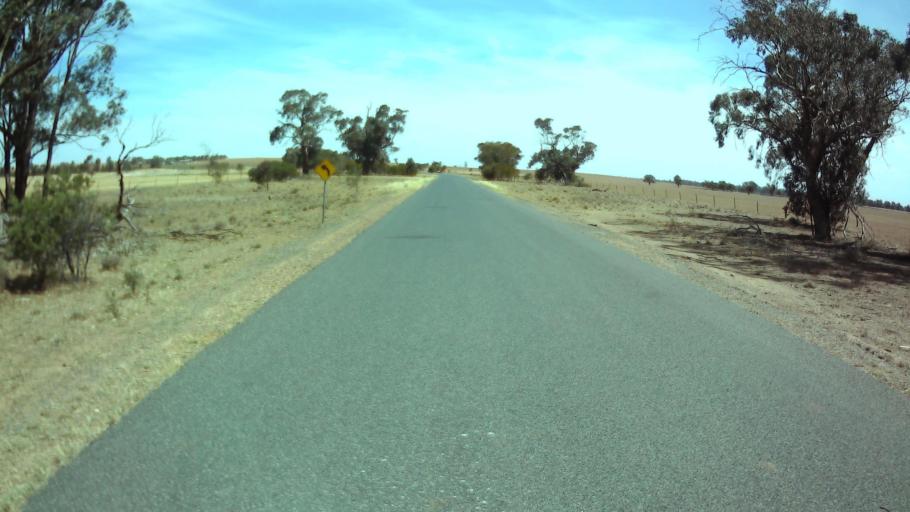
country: AU
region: New South Wales
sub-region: Weddin
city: Grenfell
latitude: -33.8848
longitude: 147.7422
